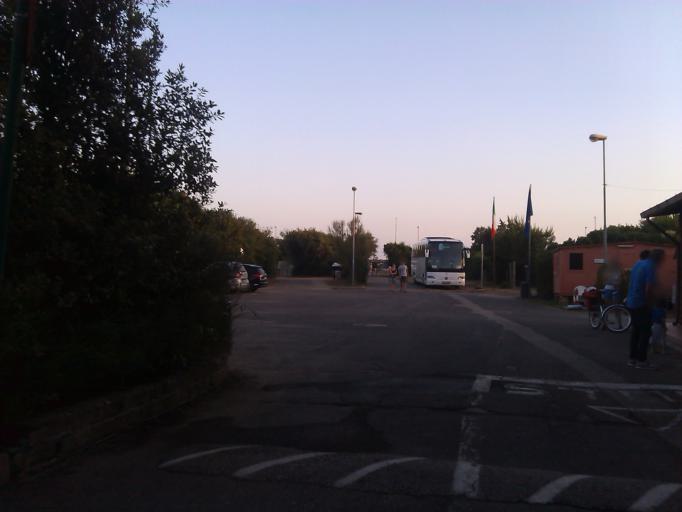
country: IT
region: Latium
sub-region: Citta metropolitana di Roma Capitale
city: Acilia-Castel Fusano-Ostia Antica
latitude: 41.7060
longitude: 12.3401
